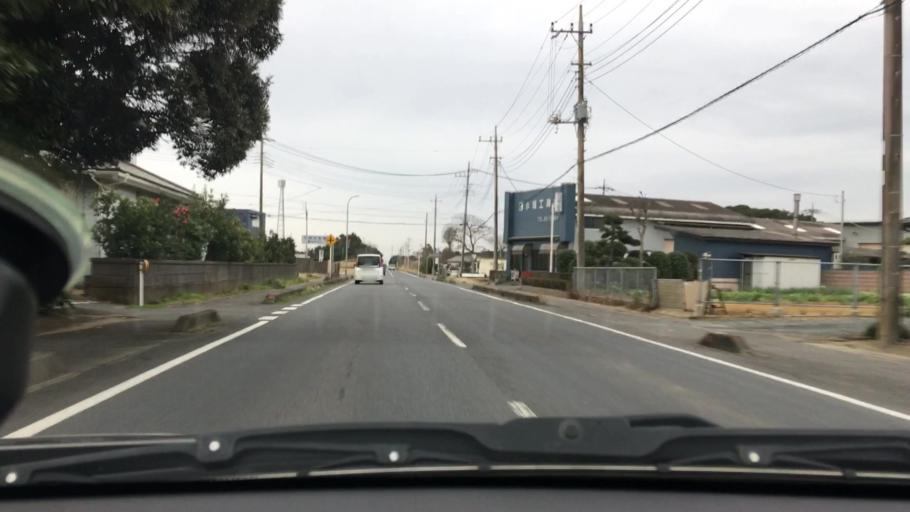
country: JP
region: Chiba
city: Omigawa
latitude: 35.8700
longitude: 140.6515
